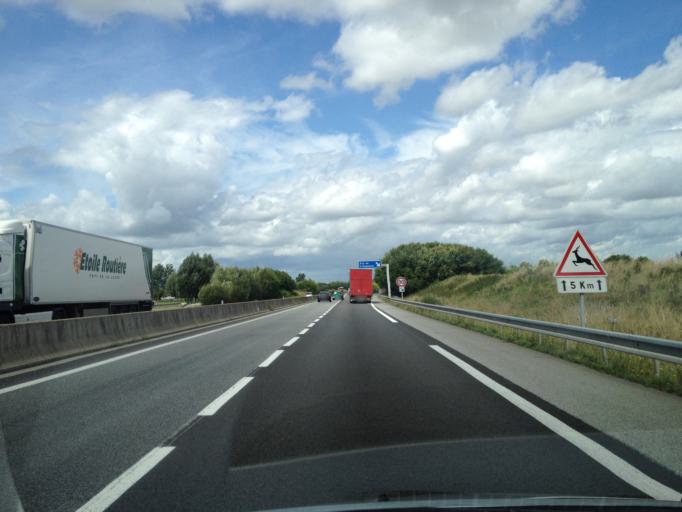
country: FR
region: Pays de la Loire
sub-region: Departement de la Sarthe
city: Beaumont-sur-Sarthe
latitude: 48.2398
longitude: 0.1667
